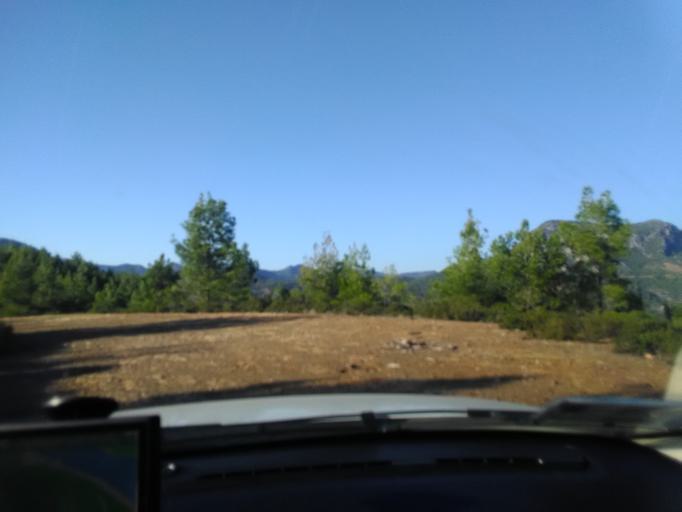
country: TR
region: Antalya
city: Gazipasa
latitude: 36.3075
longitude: 32.3975
